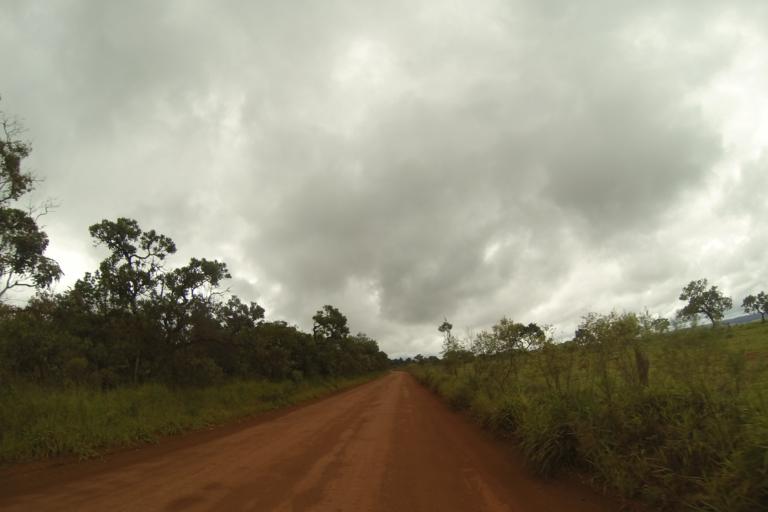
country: BR
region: Minas Gerais
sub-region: Campos Altos
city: Campos Altos
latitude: -19.8081
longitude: -46.3488
